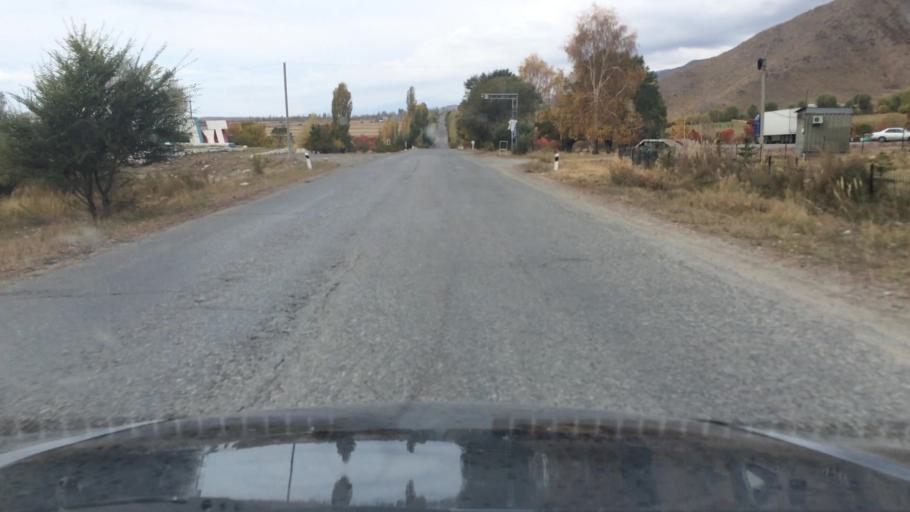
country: KG
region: Ysyk-Koel
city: Tyup
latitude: 42.7354
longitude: 77.9724
